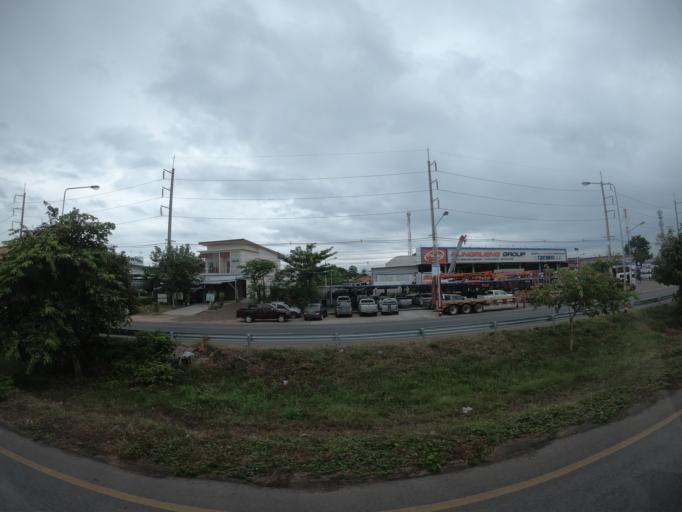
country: TH
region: Roi Et
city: Roi Et
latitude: 16.0494
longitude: 103.6210
